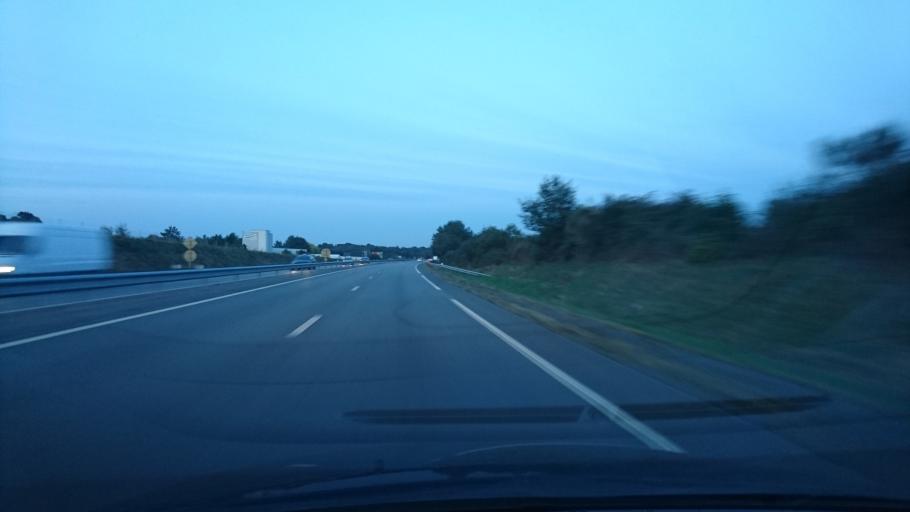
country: FR
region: Brittany
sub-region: Departement d'Ille-et-Vilaine
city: Chavagne
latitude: 48.0212
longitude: -1.7897
